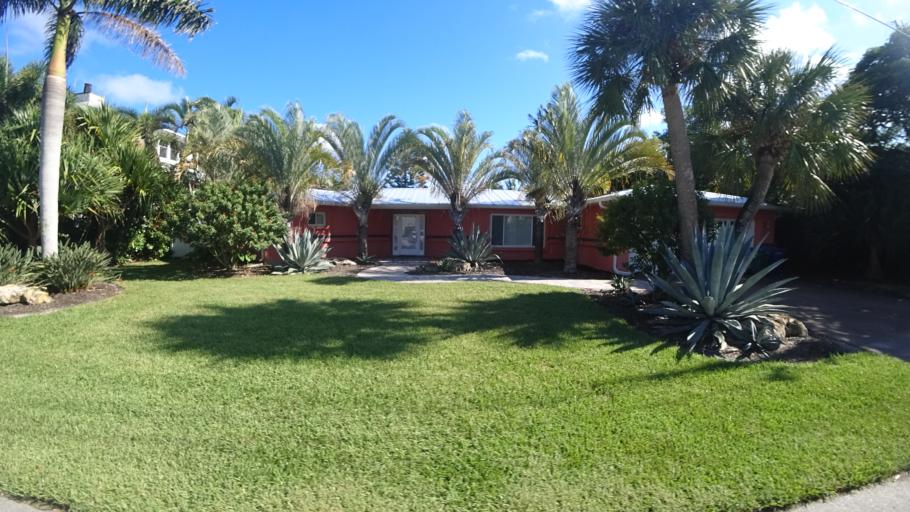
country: US
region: Florida
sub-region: Manatee County
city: Anna Maria
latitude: 27.5218
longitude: -82.7195
